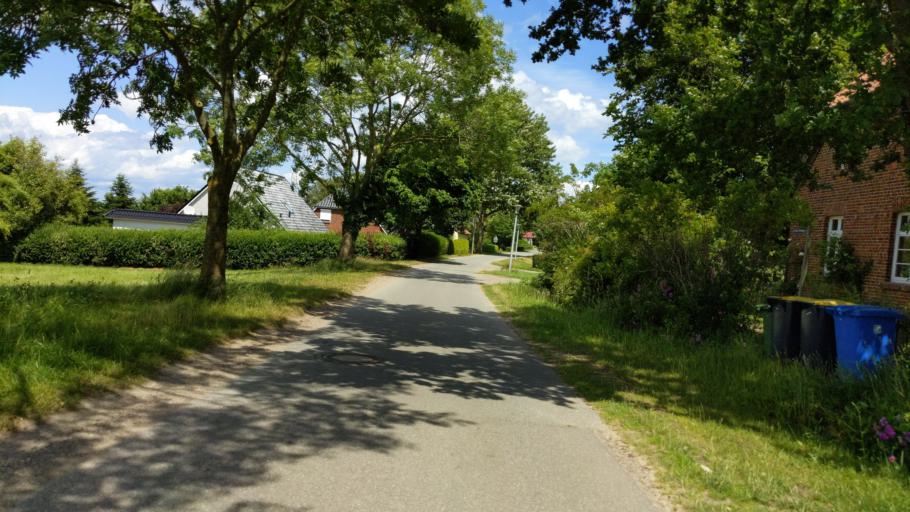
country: DE
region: Mecklenburg-Vorpommern
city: Kalkhorst
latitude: 53.9986
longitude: 11.0834
